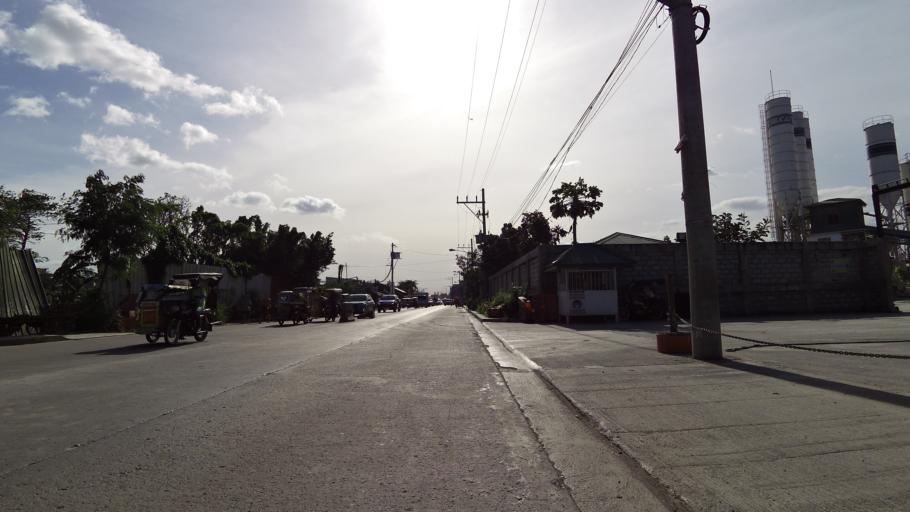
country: PH
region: Calabarzon
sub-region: Province of Rizal
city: Taytay
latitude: 14.5514
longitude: 121.1233
